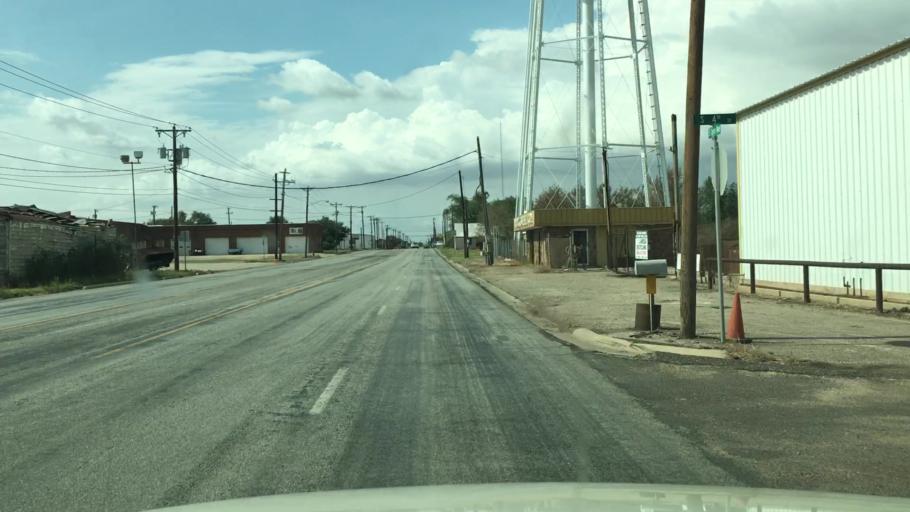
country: US
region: Texas
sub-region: Dawson County
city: Lamesa
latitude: 32.7297
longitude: -101.9480
